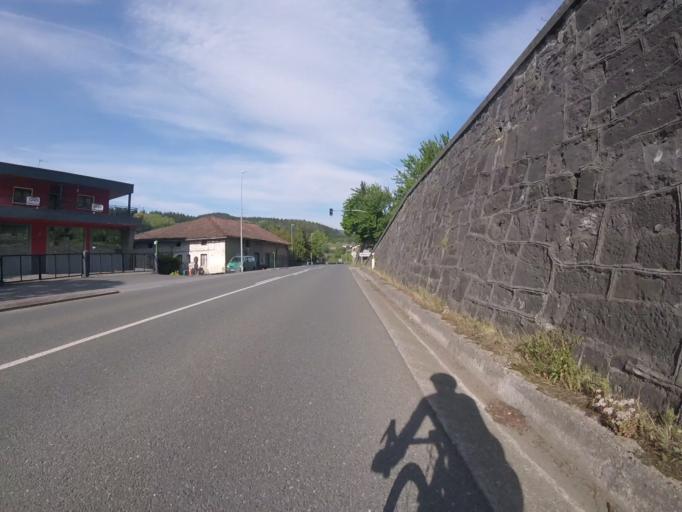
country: ES
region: Basque Country
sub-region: Provincia de Guipuzcoa
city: Ormaiztegui
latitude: 43.0419
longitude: -2.2492
